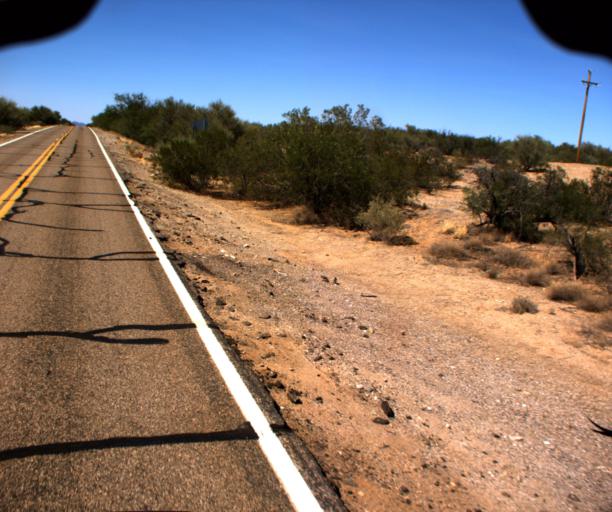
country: US
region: Arizona
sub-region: Pima County
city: Three Points
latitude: 31.9447
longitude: -111.3905
